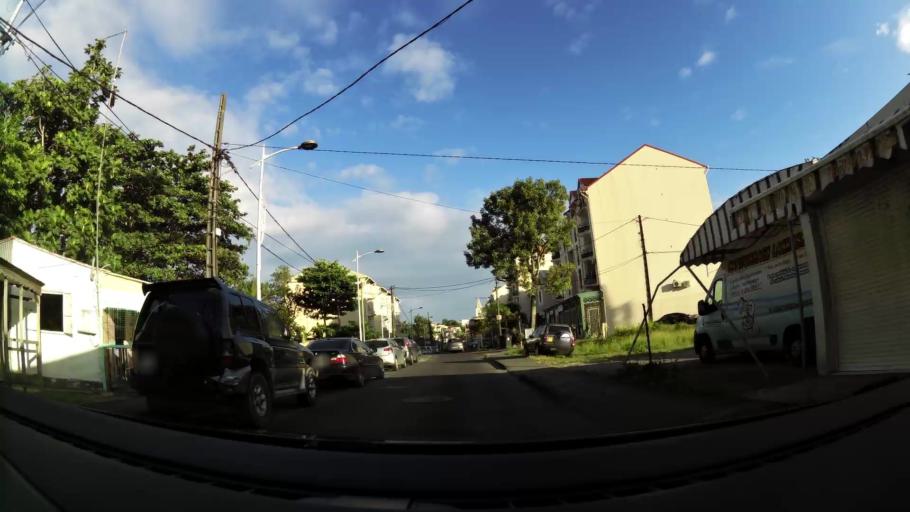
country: GP
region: Guadeloupe
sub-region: Guadeloupe
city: Pointe-a-Pitre
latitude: 16.2307
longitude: -61.5314
